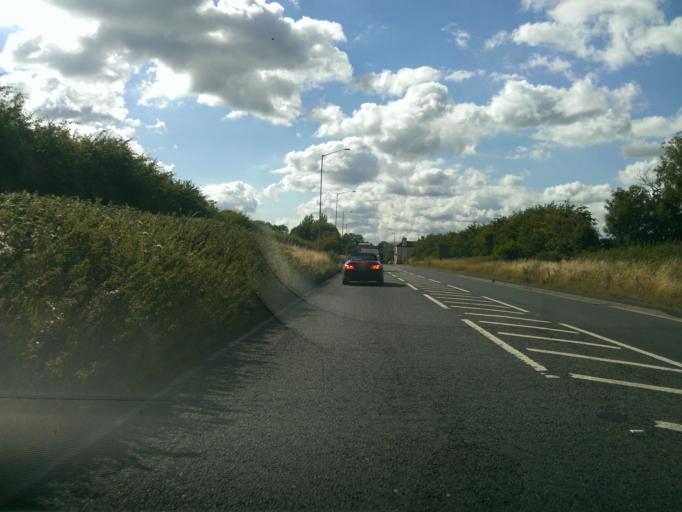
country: GB
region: England
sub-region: Warwickshire
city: Hartshill
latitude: 52.5682
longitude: -1.5156
